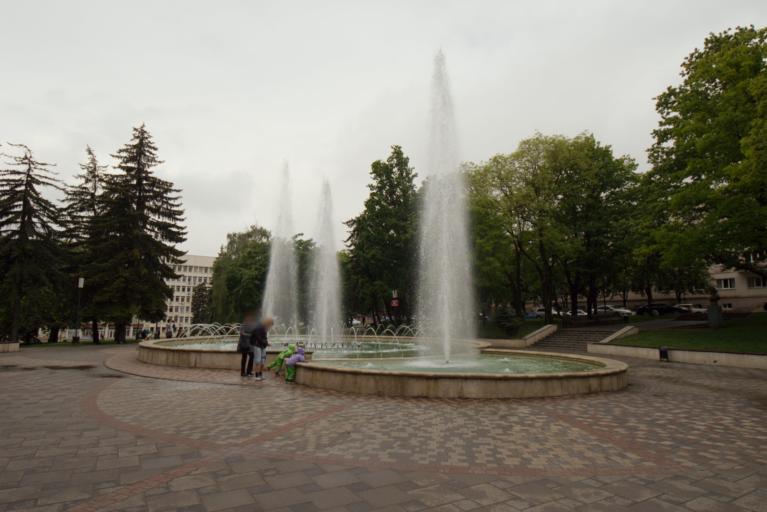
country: RU
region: Stavropol'skiy
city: Pyatigorsk
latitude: 44.0398
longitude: 43.0722
